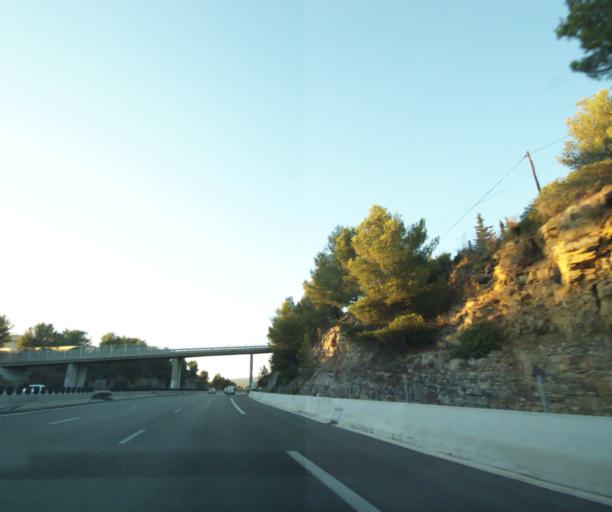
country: FR
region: Provence-Alpes-Cote d'Azur
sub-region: Departement des Bouches-du-Rhone
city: Ceyreste
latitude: 43.1986
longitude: 5.6378
